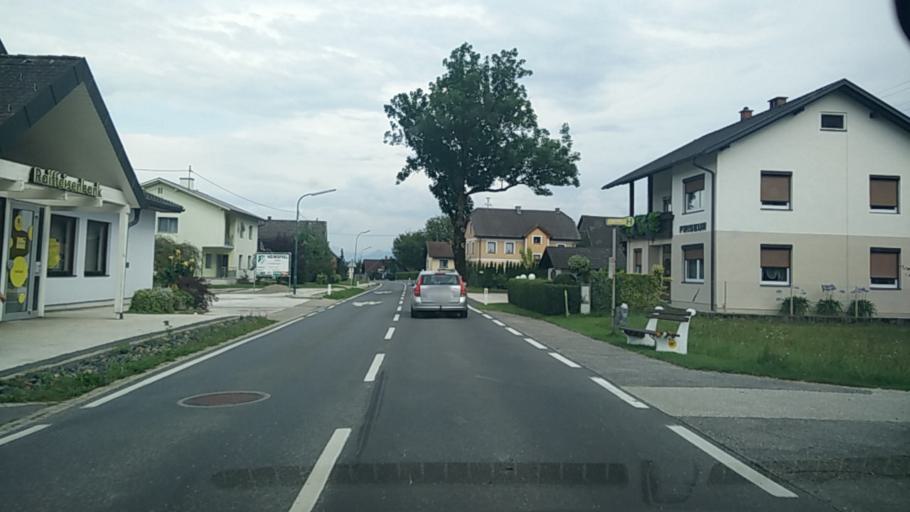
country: AT
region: Carinthia
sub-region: Politischer Bezirk Klagenfurt Land
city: Grafenstein
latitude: 46.6342
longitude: 14.5349
